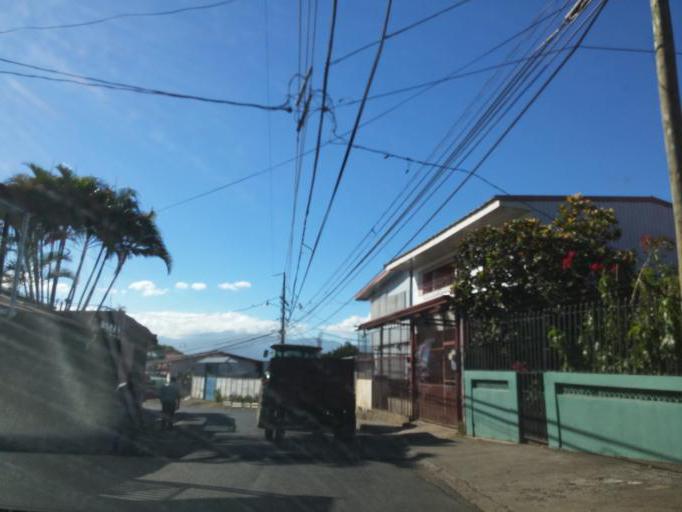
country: CR
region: Alajuela
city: Alajuela
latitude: 10.0320
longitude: -84.2042
